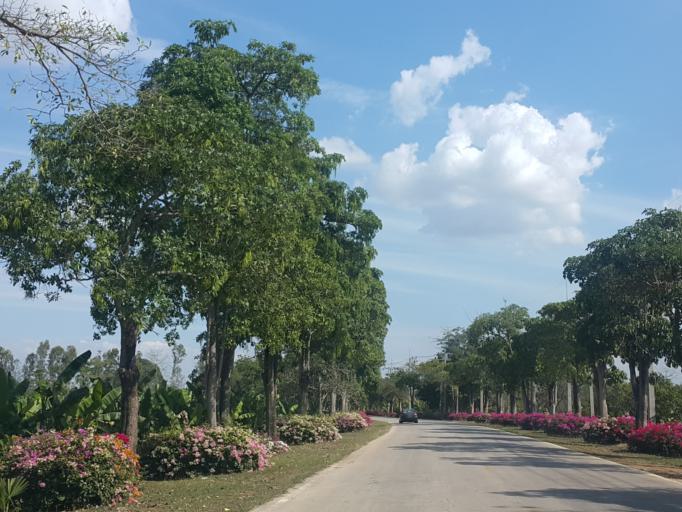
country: TH
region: Sukhothai
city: Si Samrong
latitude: 17.2284
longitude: 99.8388
